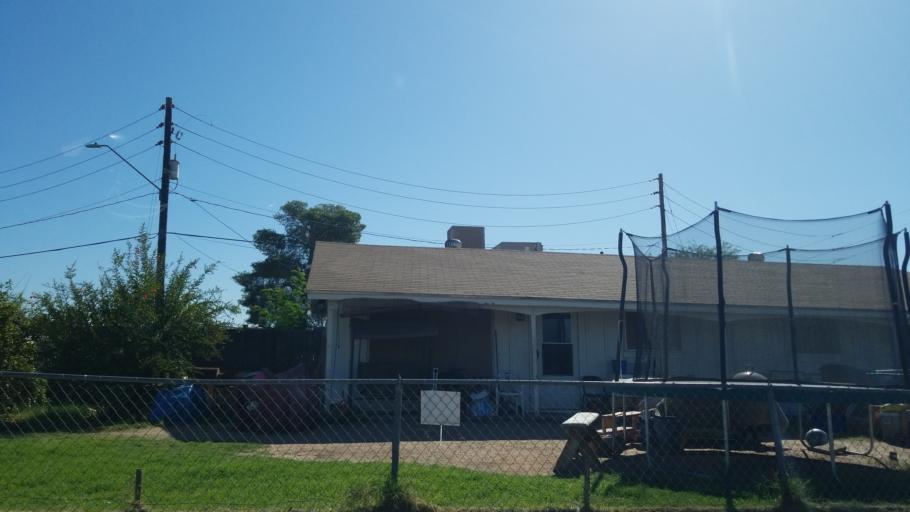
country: US
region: Arizona
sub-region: Maricopa County
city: Glendale
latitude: 33.4708
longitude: -112.1654
